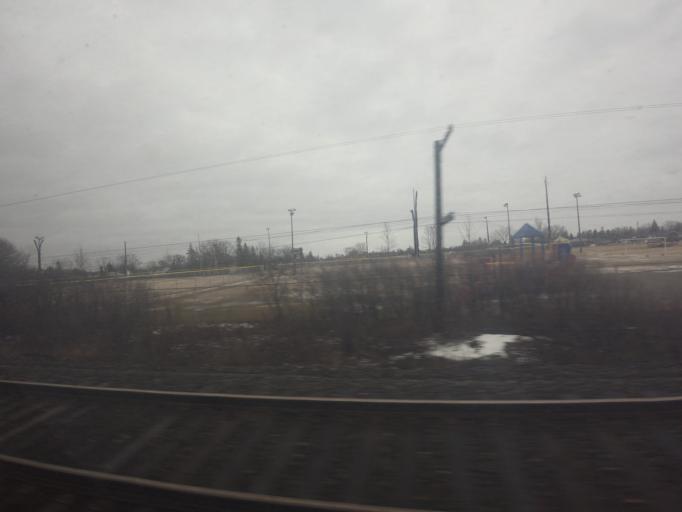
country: CA
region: Ontario
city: Kingston
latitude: 44.2275
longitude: -76.6401
